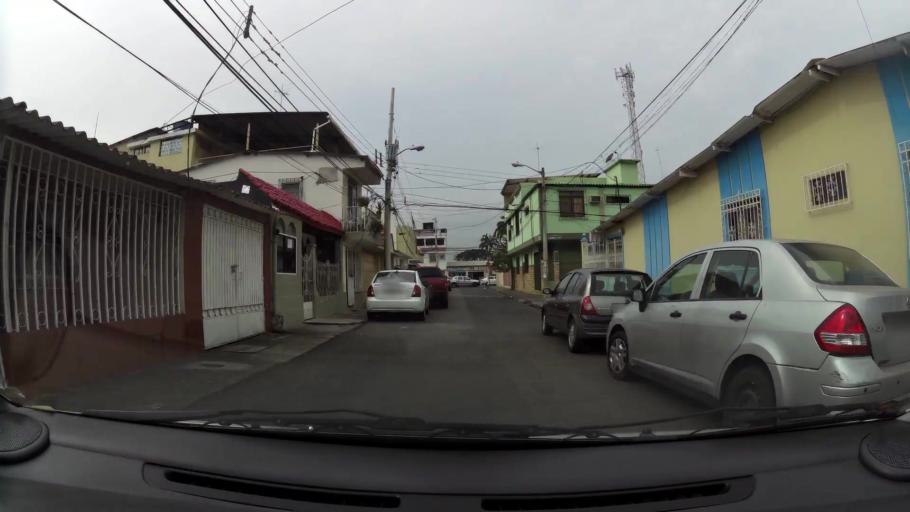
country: EC
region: Guayas
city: Eloy Alfaro
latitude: -2.1384
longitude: -79.8981
